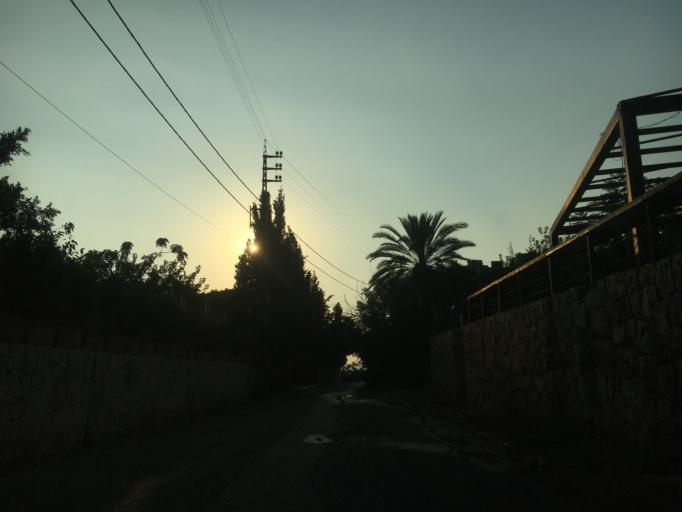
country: LB
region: Mont-Liban
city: Jbail
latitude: 34.1367
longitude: 35.6409
